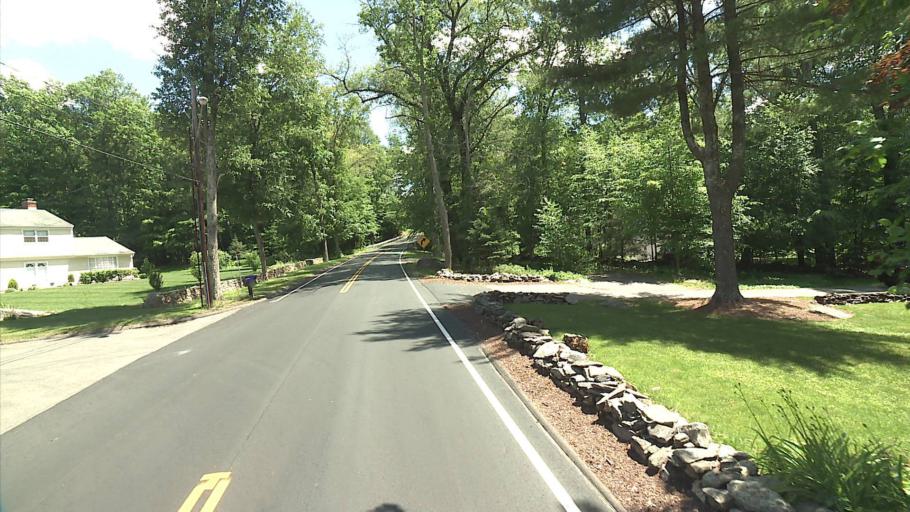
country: US
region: Connecticut
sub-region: Tolland County
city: Somers
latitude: 41.9923
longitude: -72.4272
